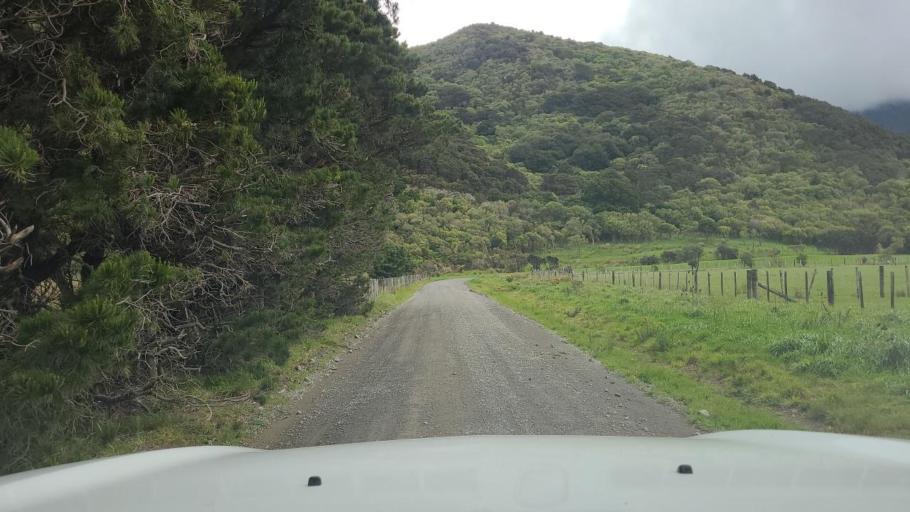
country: NZ
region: Wellington
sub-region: Upper Hutt City
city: Upper Hutt
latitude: -41.1692
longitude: 175.2381
